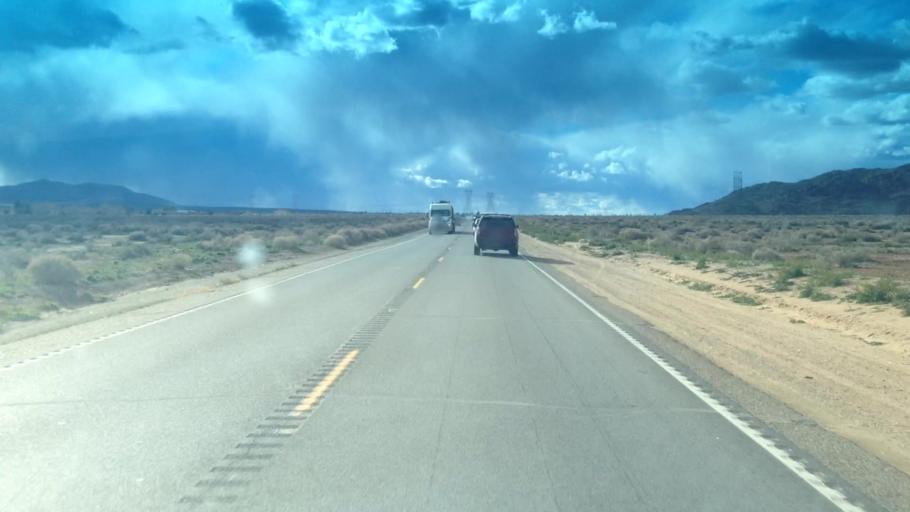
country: US
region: California
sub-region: San Bernardino County
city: Lucerne Valley
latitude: 34.4505
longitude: -117.0378
